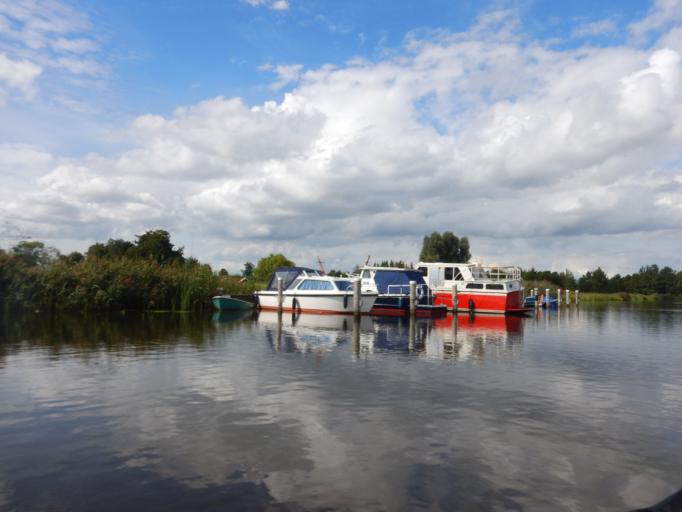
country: NL
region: Groningen
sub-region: Gemeente  Oldambt
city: Winschoten
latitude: 53.1873
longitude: 7.0625
